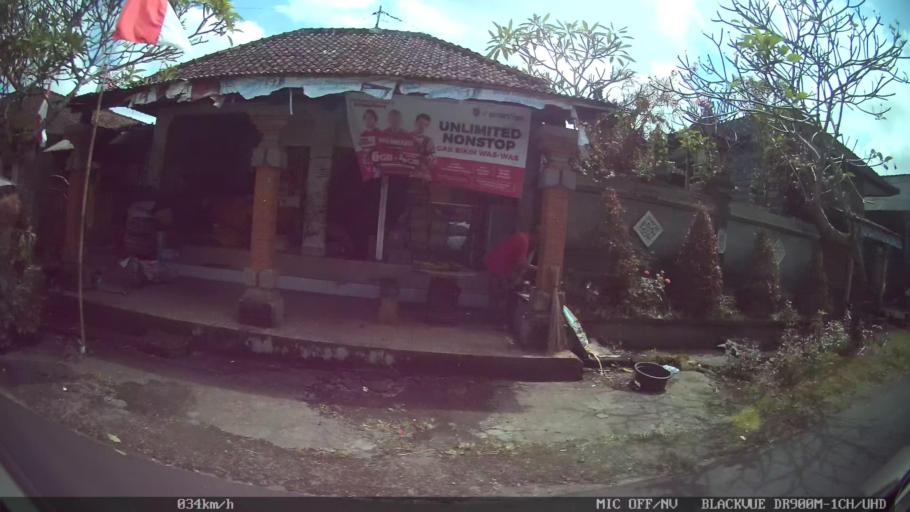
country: ID
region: Bali
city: Banjar Kelodan
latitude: -8.5101
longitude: 115.3807
